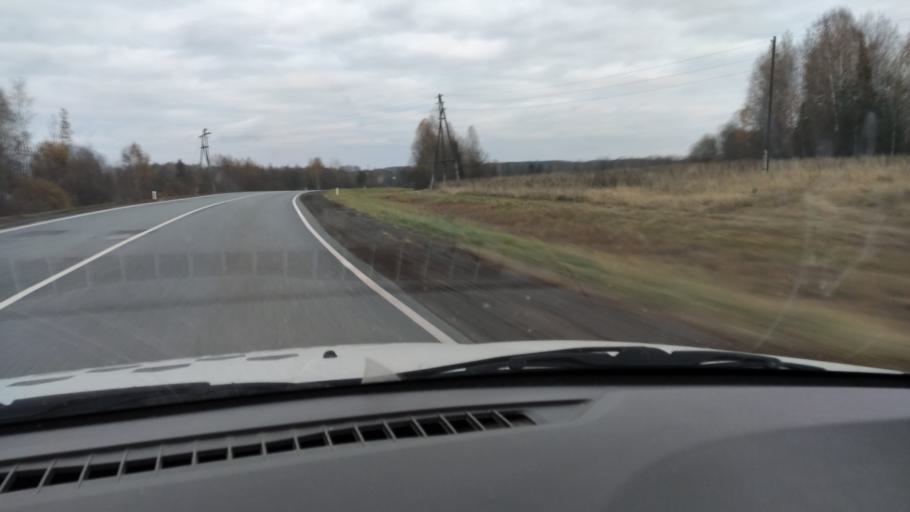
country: RU
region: Kirov
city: Belorechensk
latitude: 58.8082
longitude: 52.4622
